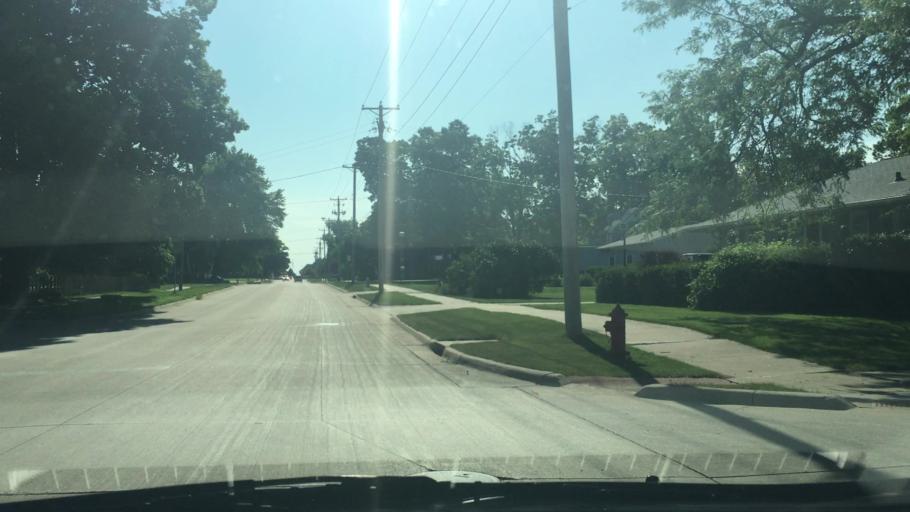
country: US
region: Iowa
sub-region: Johnson County
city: North Liberty
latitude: 41.7485
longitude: -91.6025
